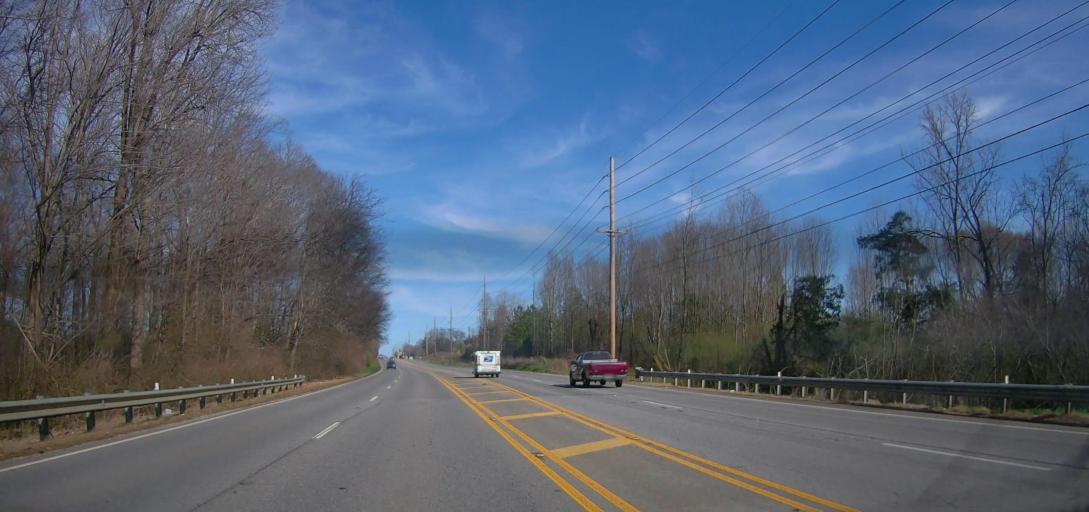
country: US
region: Alabama
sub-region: Limestone County
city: Athens
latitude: 34.7914
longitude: -87.0325
